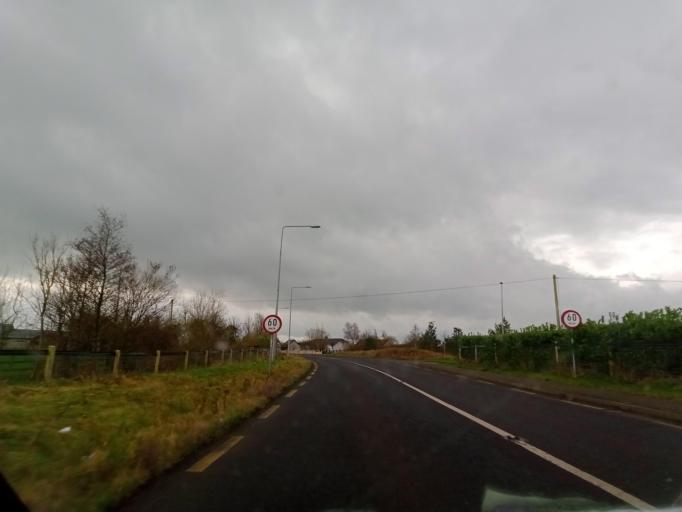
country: IE
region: Munster
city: Thurles
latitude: 52.6200
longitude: -7.7747
